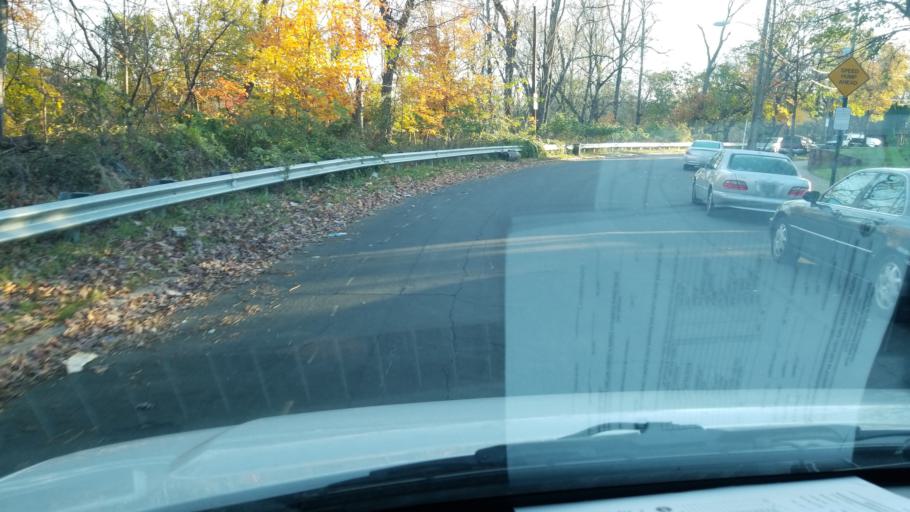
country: US
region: Maryland
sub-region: Prince George's County
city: Glassmanor
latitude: 38.8488
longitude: -77.0021
